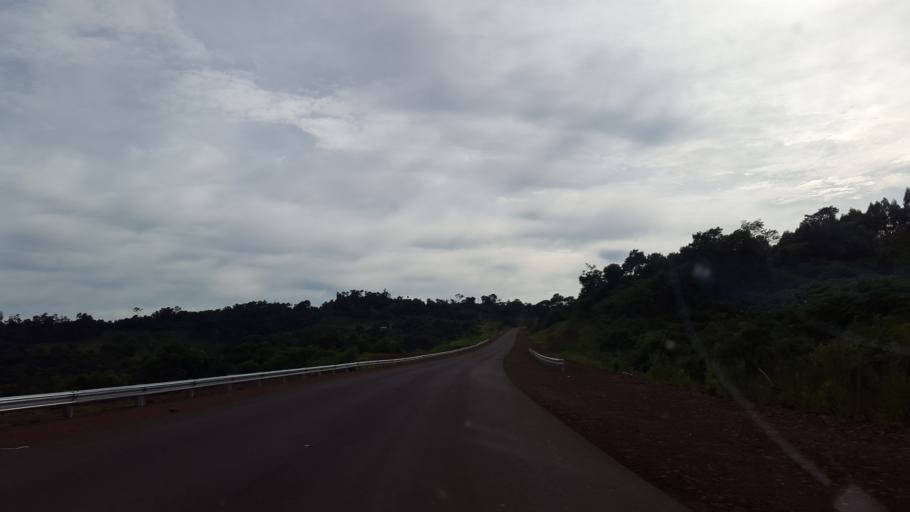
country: AR
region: Misiones
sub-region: Departamento de San Pedro
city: San Pedro
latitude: -26.4557
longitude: -53.8700
